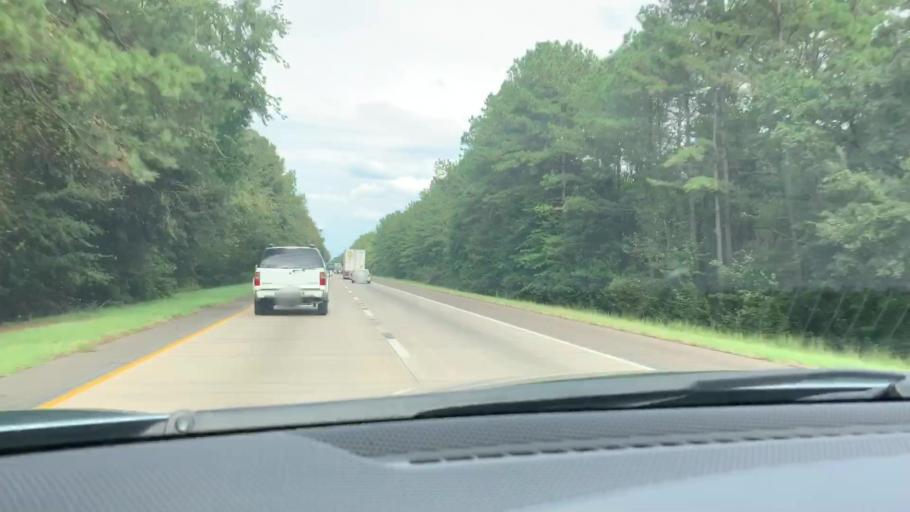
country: US
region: South Carolina
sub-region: Hampton County
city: Yemassee
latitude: 32.7635
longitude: -80.8129
